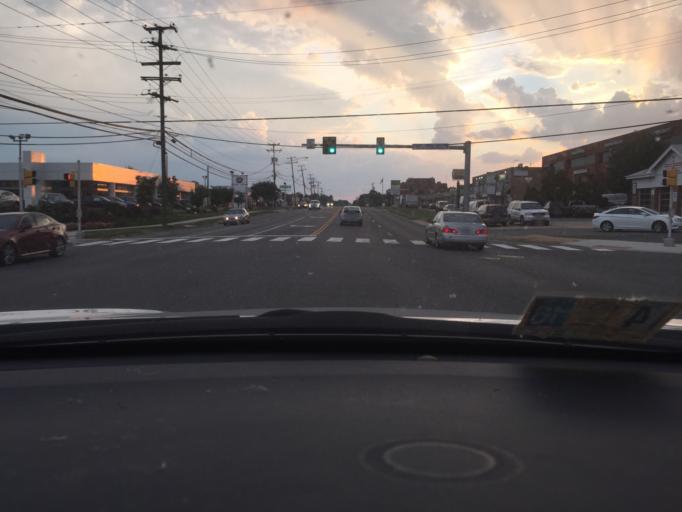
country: US
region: Virginia
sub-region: Fairfax County
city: Merrifield
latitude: 38.8737
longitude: -77.2359
